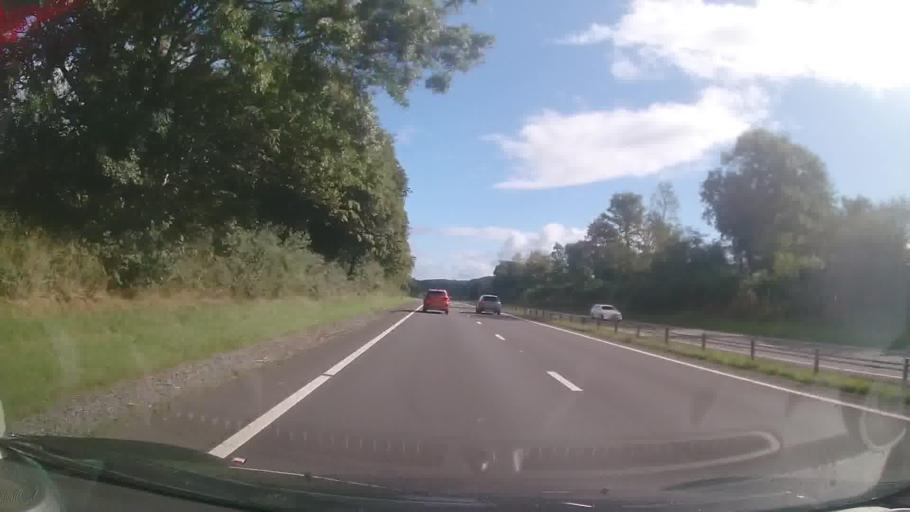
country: GB
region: Wales
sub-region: Carmarthenshire
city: Carmarthen
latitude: 51.8406
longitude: -4.2729
